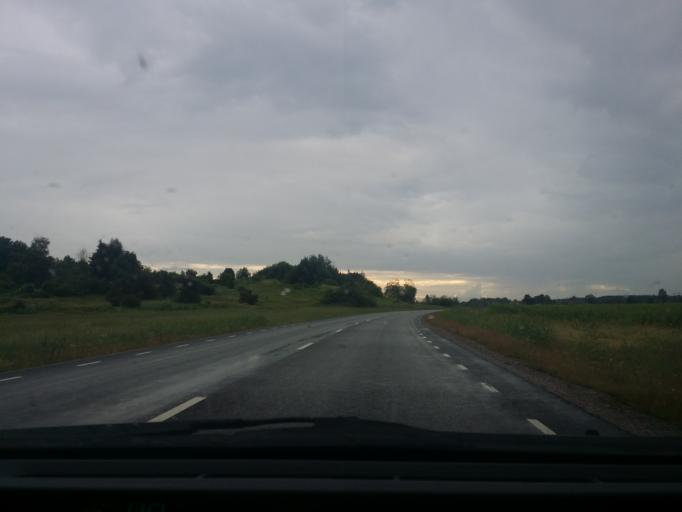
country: SE
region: Vaestmanland
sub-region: Arboga Kommun
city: Arboga
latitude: 59.4028
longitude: 15.8659
